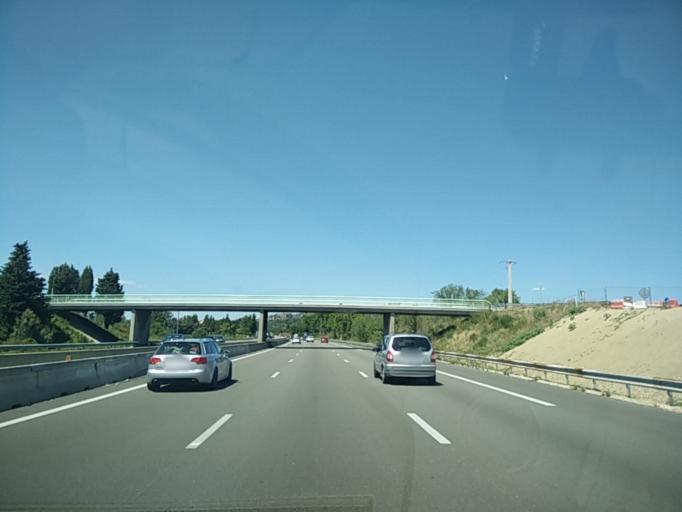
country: FR
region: Provence-Alpes-Cote d'Azur
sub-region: Departement du Vaucluse
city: Piolenc
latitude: 44.1836
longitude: 4.7513
